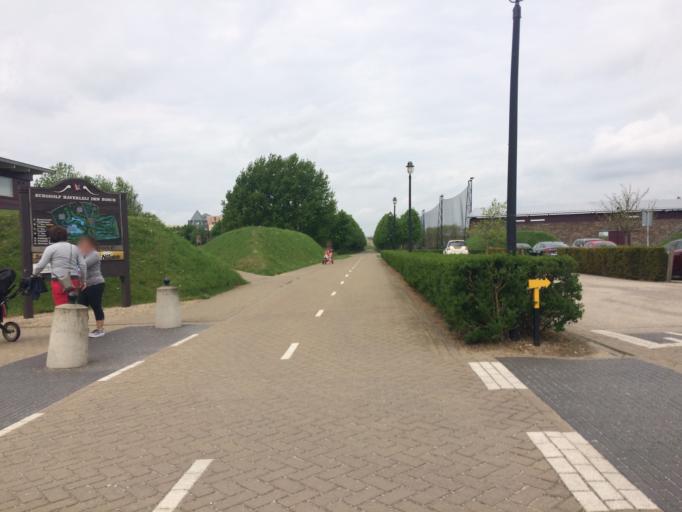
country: NL
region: Gelderland
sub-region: Gemeente Maasdriel
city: Hedel
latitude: 51.7248
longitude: 5.2554
